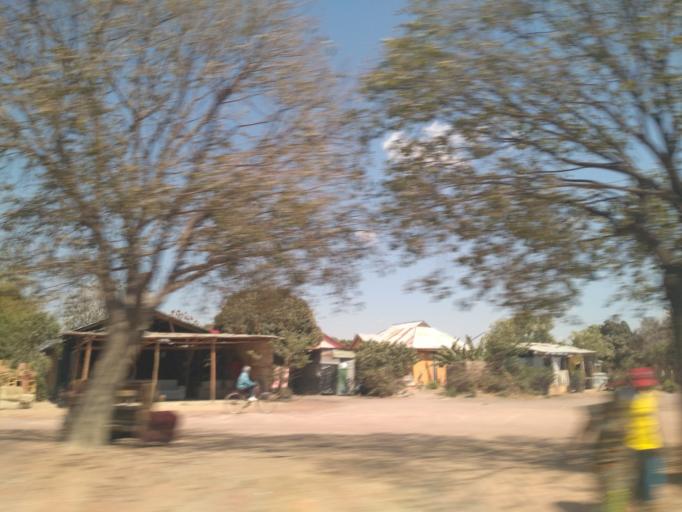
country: TZ
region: Dodoma
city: Dodoma
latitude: -6.1538
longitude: 35.7244
